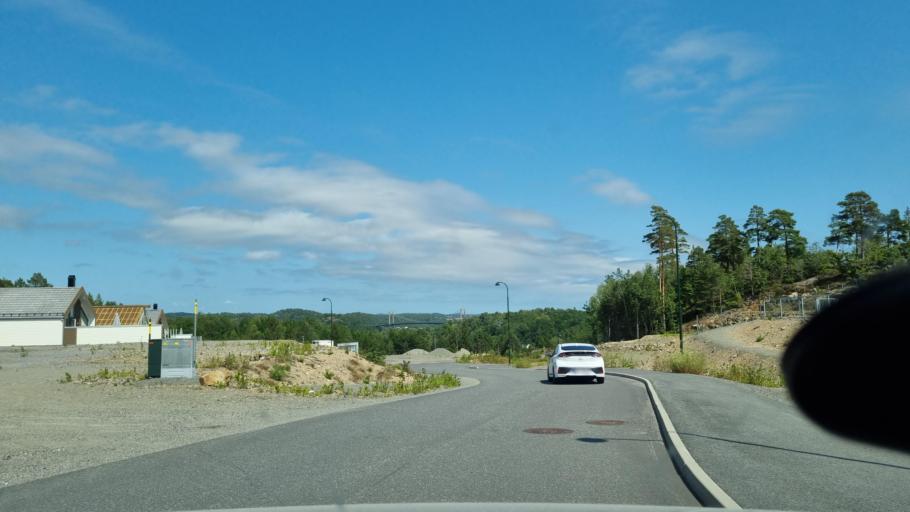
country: NO
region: Aust-Agder
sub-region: Arendal
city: Arendal
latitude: 58.4589
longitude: 8.8136
